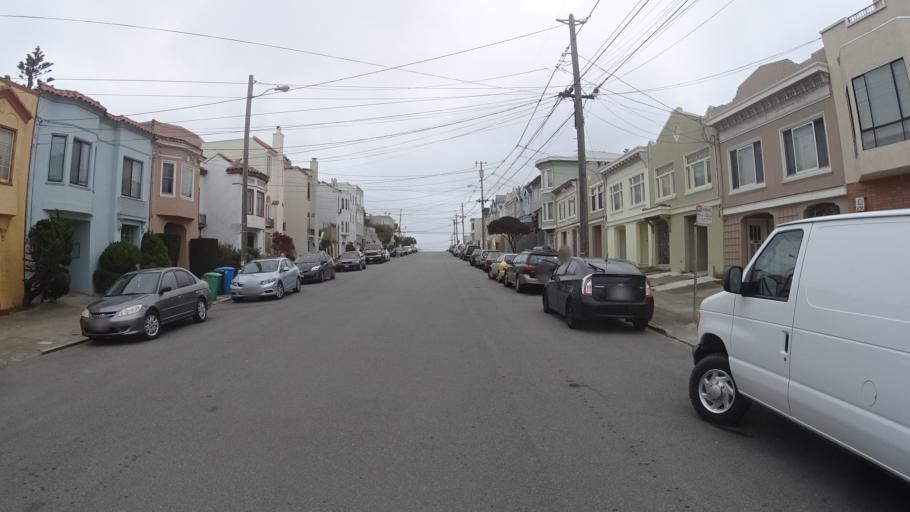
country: US
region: California
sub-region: San Francisco County
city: San Francisco
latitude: 37.7765
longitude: -122.4888
